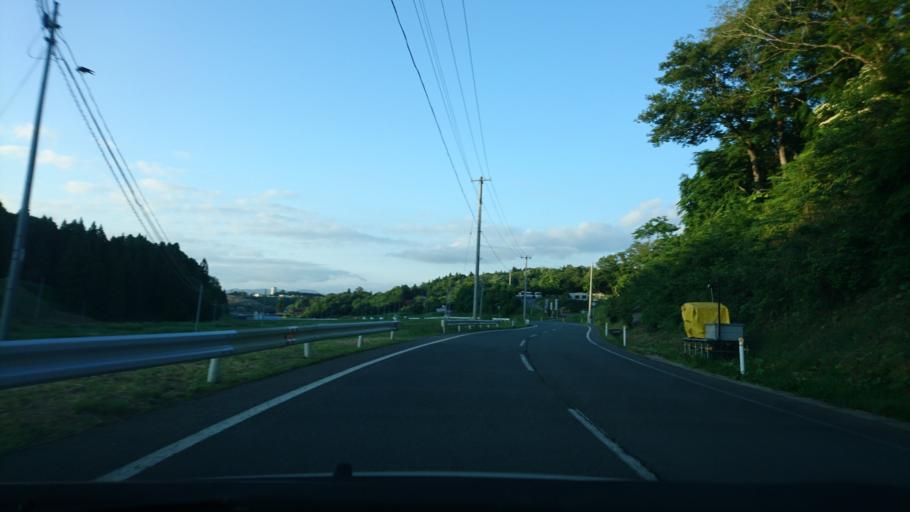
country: JP
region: Iwate
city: Ichinoseki
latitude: 38.8921
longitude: 141.1575
